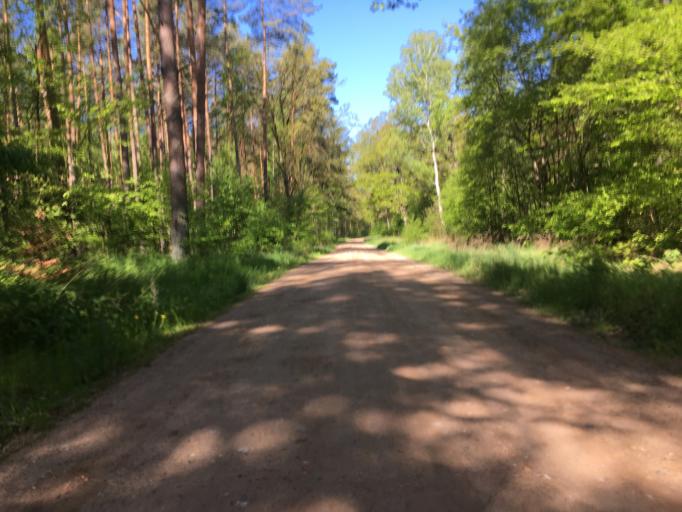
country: DE
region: Brandenburg
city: Liebenwalde
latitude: 52.9477
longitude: 13.4495
